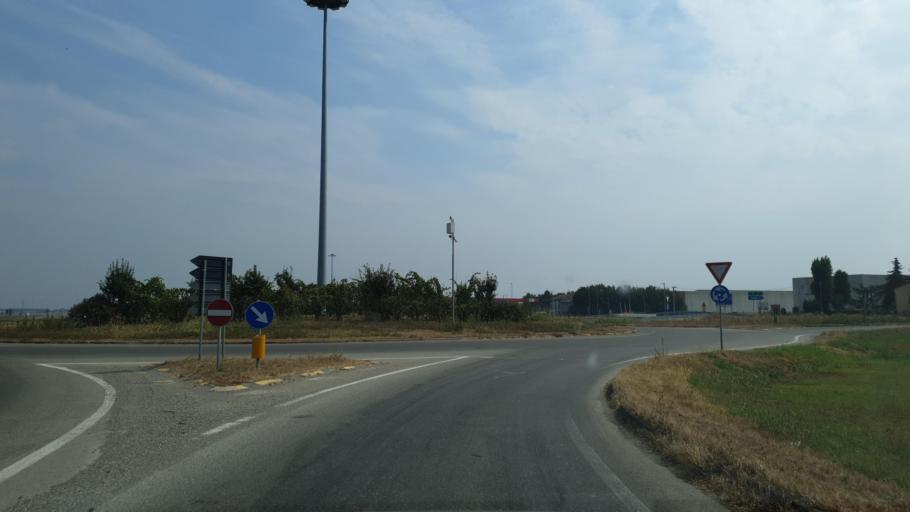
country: IT
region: Emilia-Romagna
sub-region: Provincia di Parma
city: Trecasali
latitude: 44.9160
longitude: 10.2581
